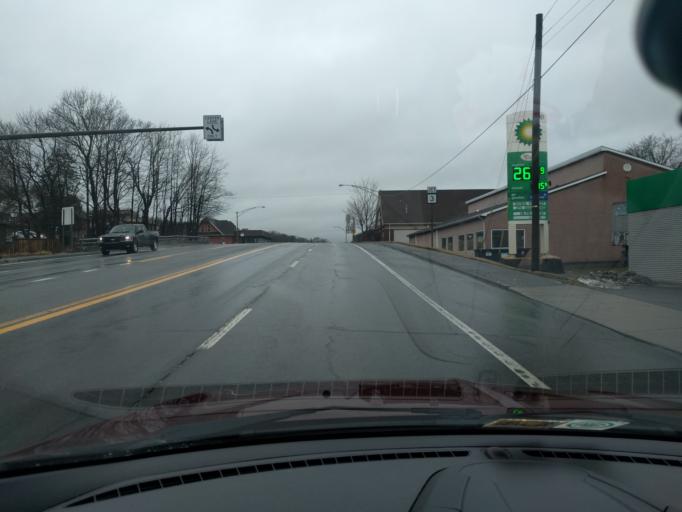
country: US
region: West Virginia
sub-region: Raleigh County
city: Beckley
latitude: 37.7726
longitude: -81.1952
